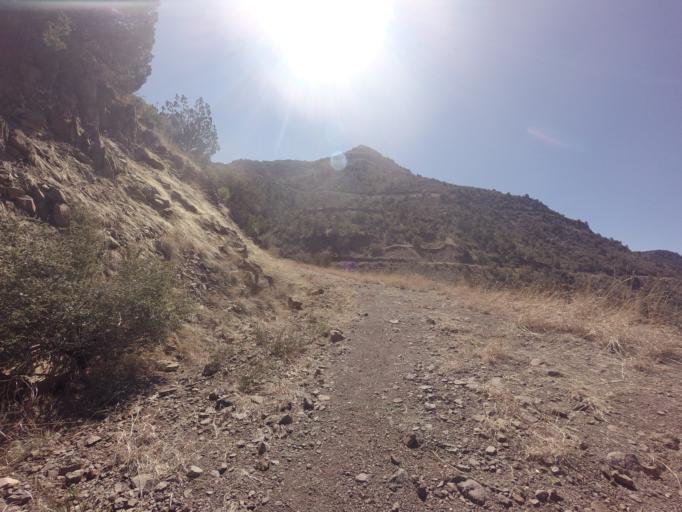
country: US
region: Arizona
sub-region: Gila County
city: Pine
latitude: 34.4067
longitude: -111.6058
